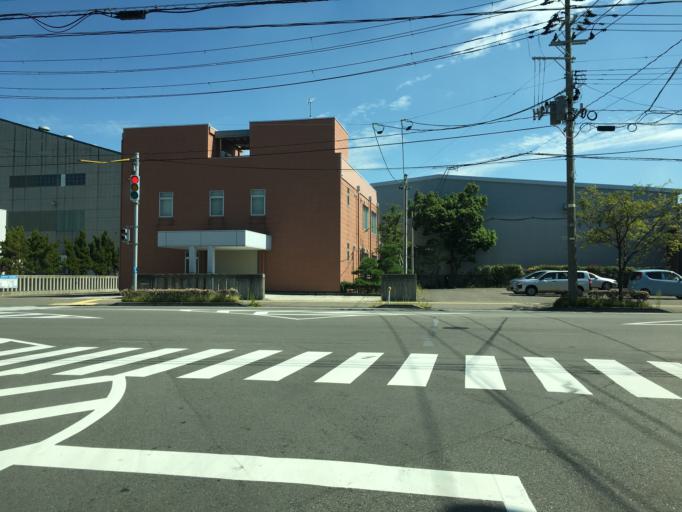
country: JP
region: Niigata
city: Niigata-shi
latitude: 37.9361
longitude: 139.0569
